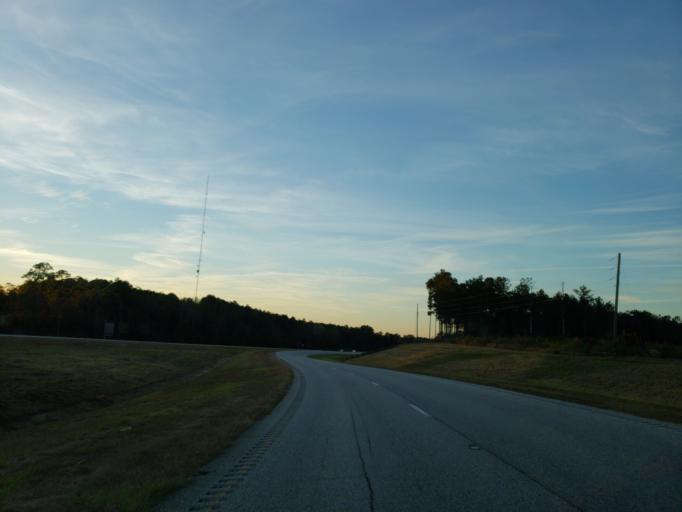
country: US
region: Mississippi
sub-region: Wayne County
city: Belmont
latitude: 31.4571
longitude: -88.4650
